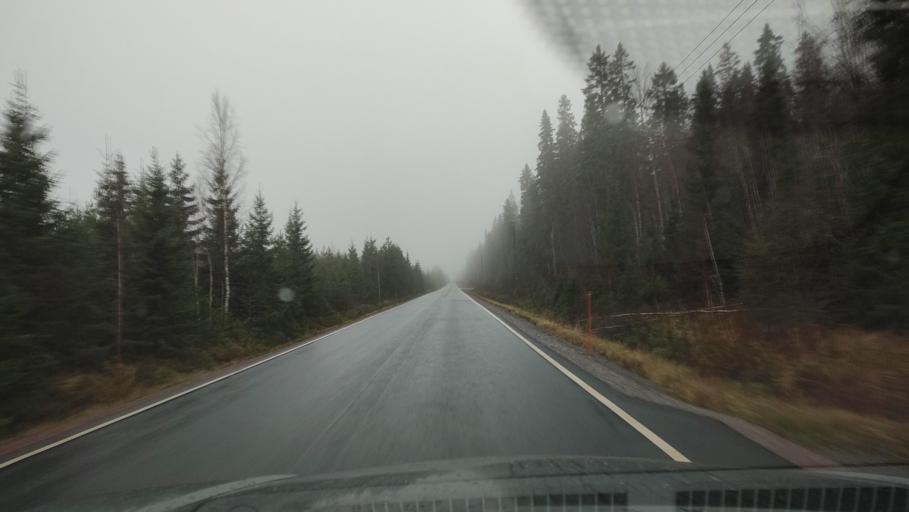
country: FI
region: Southern Ostrobothnia
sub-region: Suupohja
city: Karijoki
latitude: 62.1600
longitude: 21.7261
